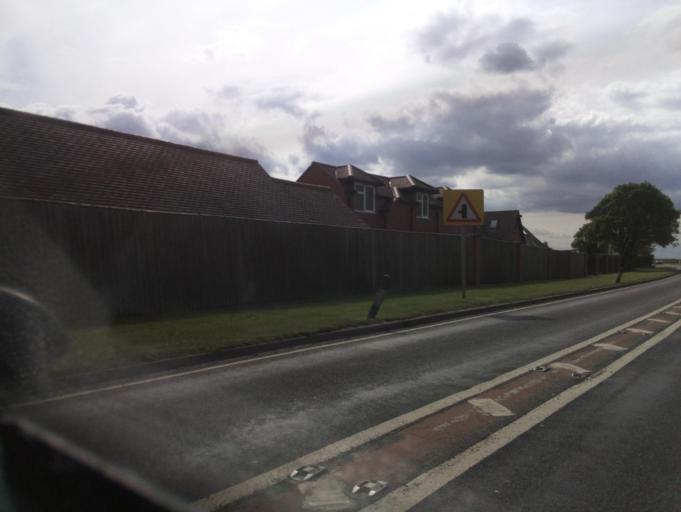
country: GB
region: England
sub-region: Worcestershire
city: Pershore
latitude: 52.1001
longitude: -2.0196
